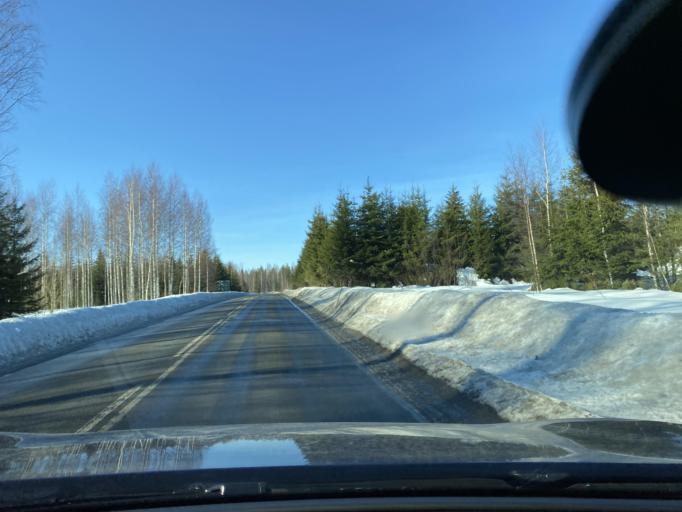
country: FI
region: Central Finland
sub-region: Joutsa
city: Joutsa
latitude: 61.7884
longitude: 26.0914
